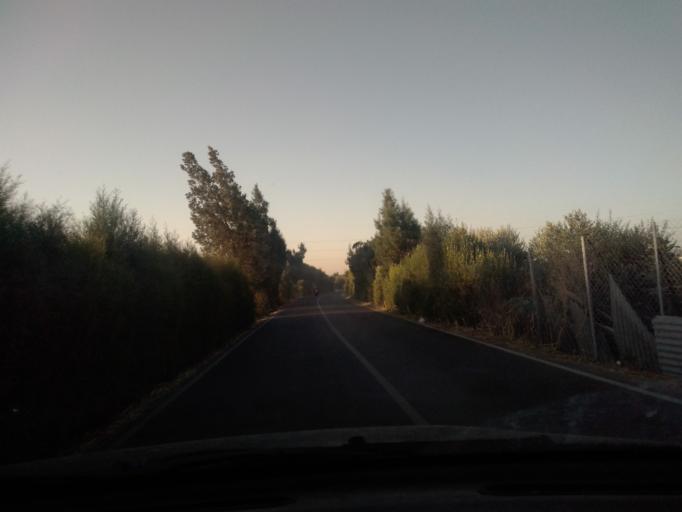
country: CY
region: Limassol
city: Ypsonas
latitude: 34.6674
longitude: 32.9615
